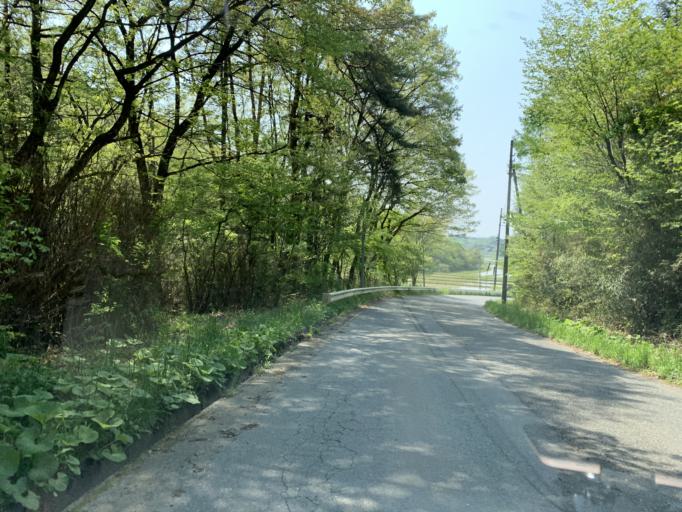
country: JP
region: Iwate
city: Ichinoseki
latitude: 38.8683
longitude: 141.0449
